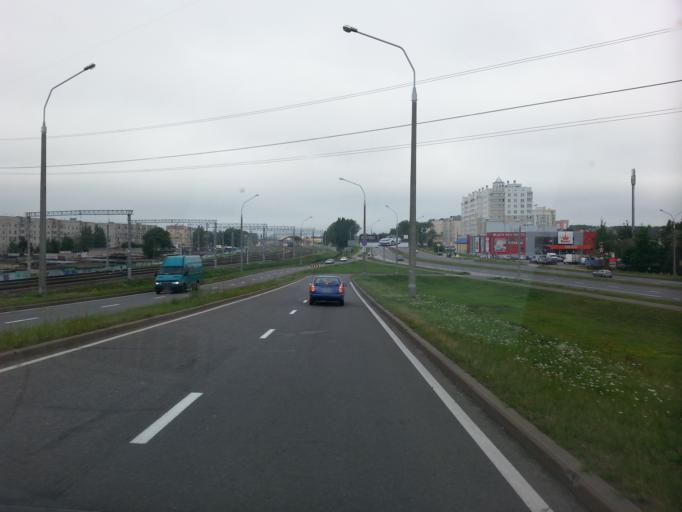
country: BY
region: Minsk
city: Zhdanovichy
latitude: 53.9442
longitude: 27.4341
